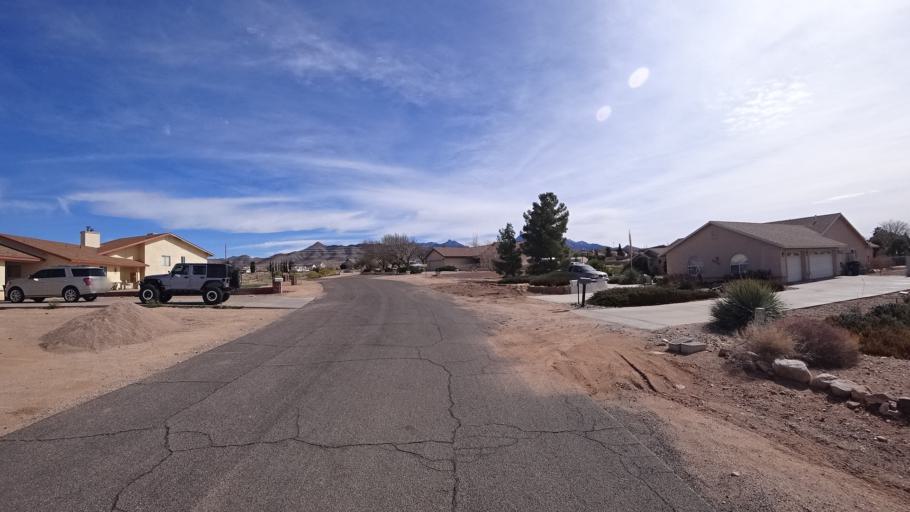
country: US
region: Arizona
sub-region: Mohave County
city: Kingman
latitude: 35.1900
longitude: -113.9879
